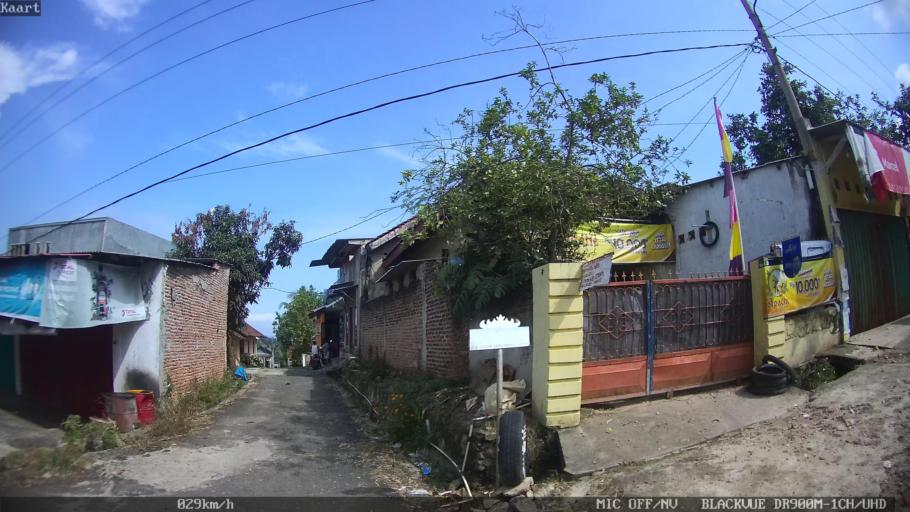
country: ID
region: Lampung
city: Bandarlampung
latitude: -5.4072
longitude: 105.2250
